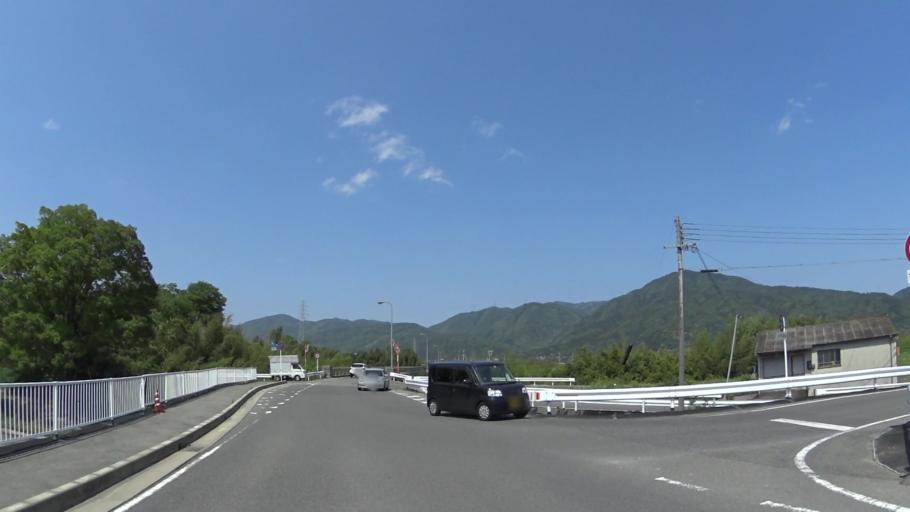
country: JP
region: Kyoto
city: Kameoka
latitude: 35.0253
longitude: 135.5701
